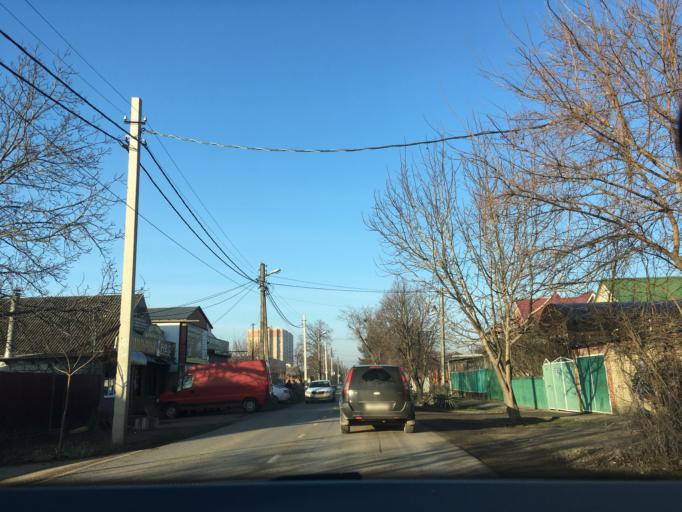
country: RU
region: Krasnodarskiy
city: Krasnodar
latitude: 45.0806
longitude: 39.0206
